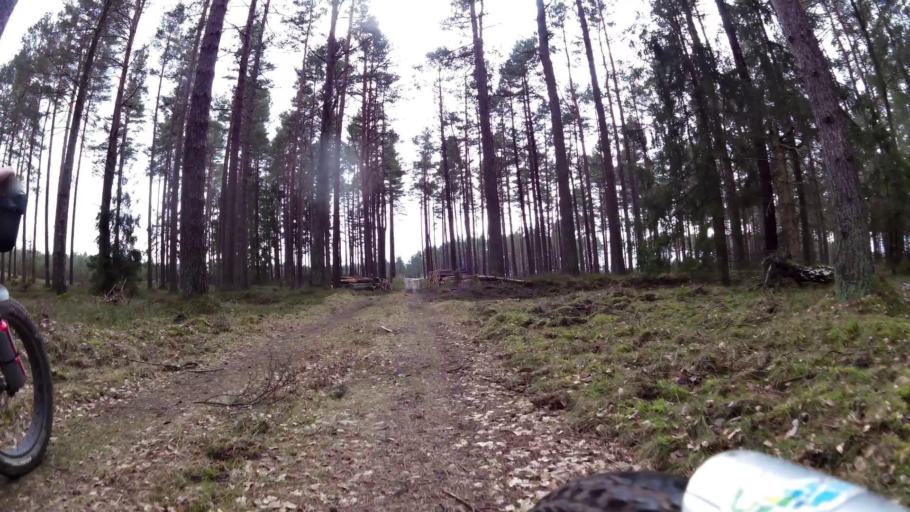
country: PL
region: Pomeranian Voivodeship
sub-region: Powiat bytowski
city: Kolczyglowy
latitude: 54.1516
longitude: 17.1802
